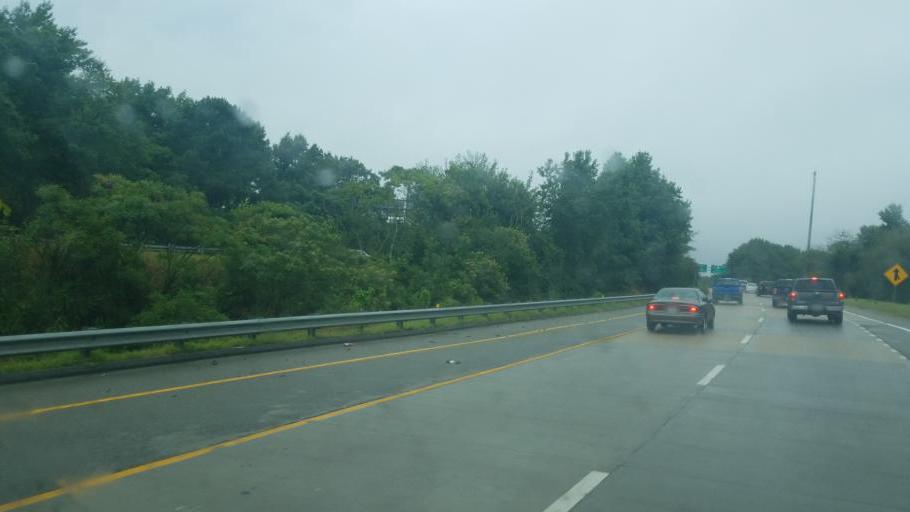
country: US
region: Virginia
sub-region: City of Chesapeake
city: Chesapeake
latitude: 36.7615
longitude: -76.2672
